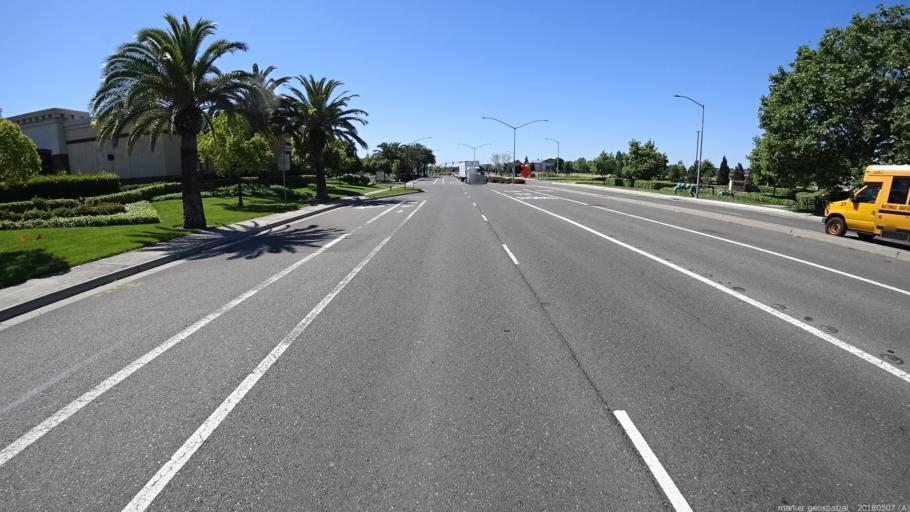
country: US
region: California
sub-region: Sacramento County
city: Sacramento
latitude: 38.6415
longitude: -121.5026
